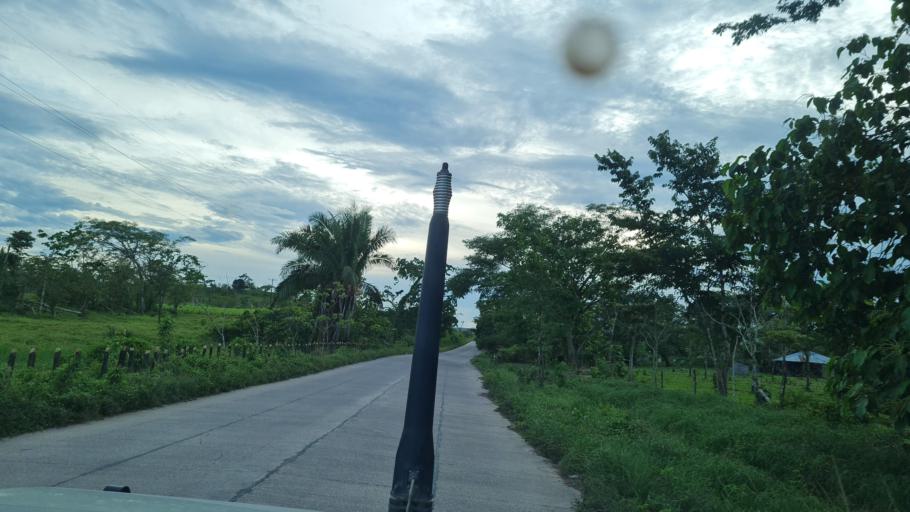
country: NI
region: Atlantico Norte (RAAN)
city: Siuna
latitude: 13.6849
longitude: -84.6009
